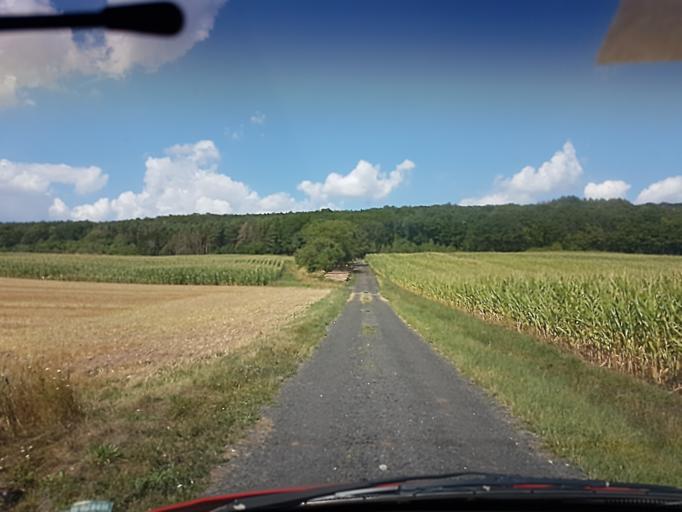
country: DE
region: Bavaria
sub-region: Regierungsbezirk Unterfranken
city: Untermerzbach
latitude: 50.1054
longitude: 10.8753
